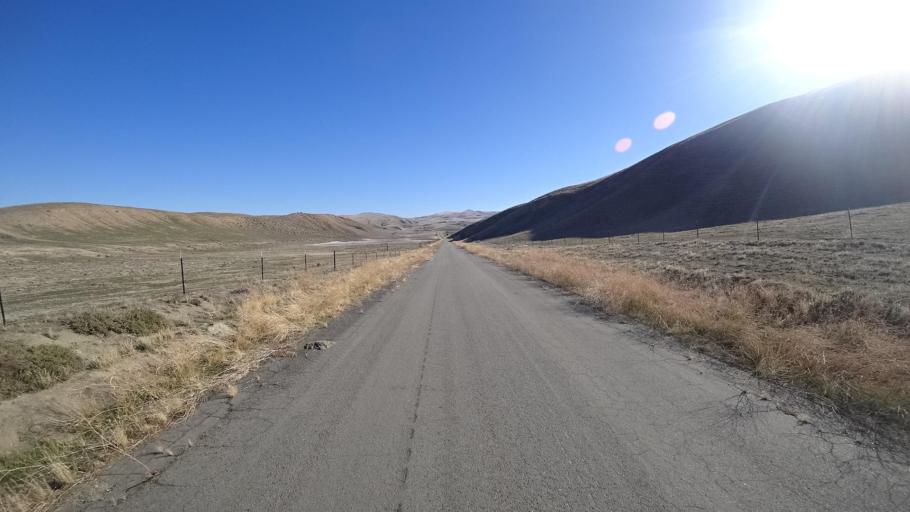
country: US
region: California
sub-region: Kern County
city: Maricopa
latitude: 34.9773
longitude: -119.4636
